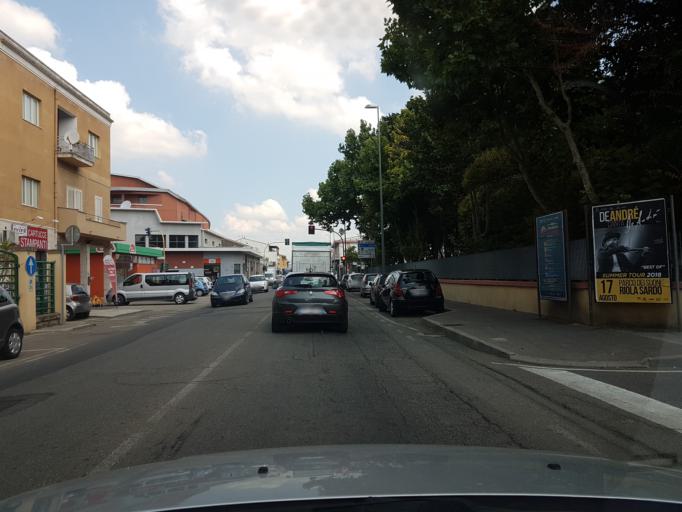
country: IT
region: Sardinia
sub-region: Provincia di Oristano
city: Oristano
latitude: 39.9072
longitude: 8.5884
